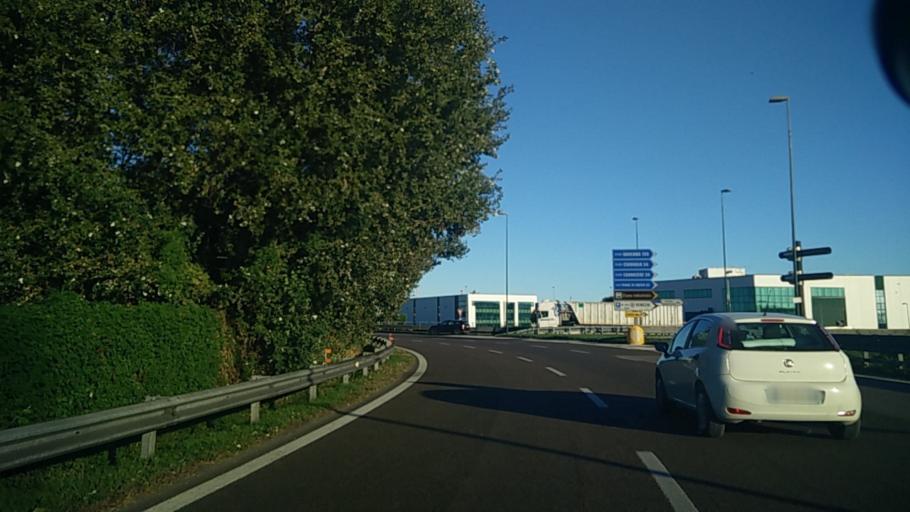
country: IT
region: Veneto
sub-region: Provincia di Venezia
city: Mestre
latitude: 45.4491
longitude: 12.2057
